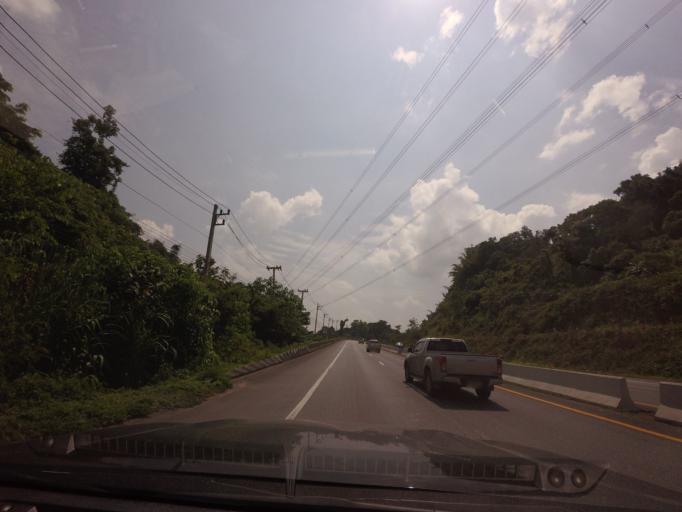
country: TH
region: Uttaradit
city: Uttaradit
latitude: 17.7688
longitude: 100.1321
